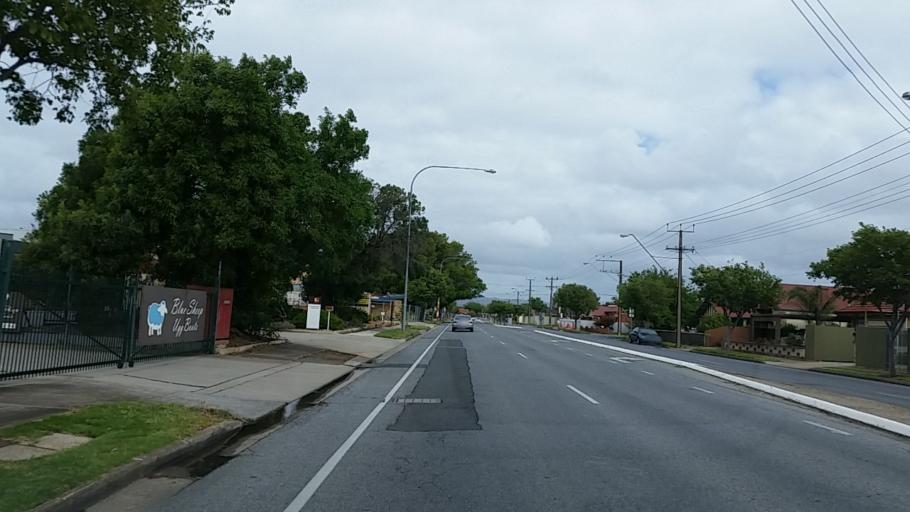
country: AU
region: South Australia
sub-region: Charles Sturt
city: Findon
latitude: -34.9017
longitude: 138.5417
